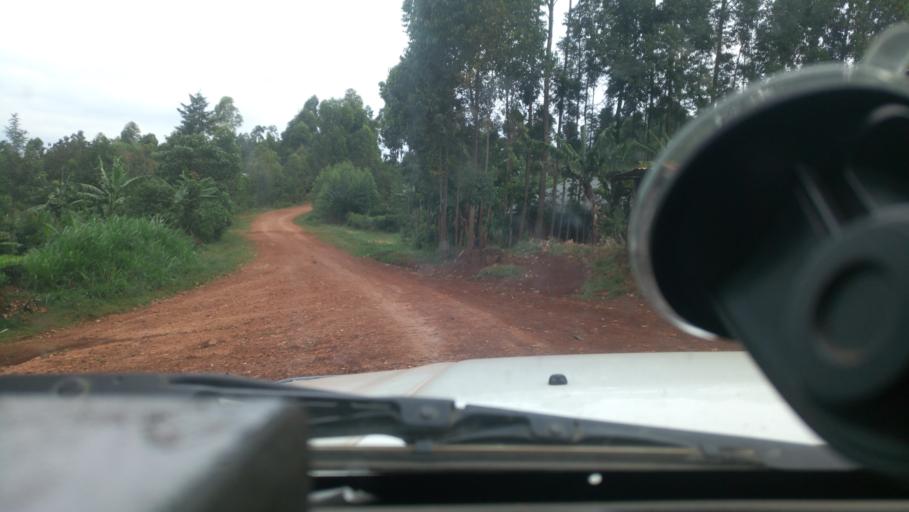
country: KE
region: Nyamira District
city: Nyamira
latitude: -0.4611
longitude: 34.9759
